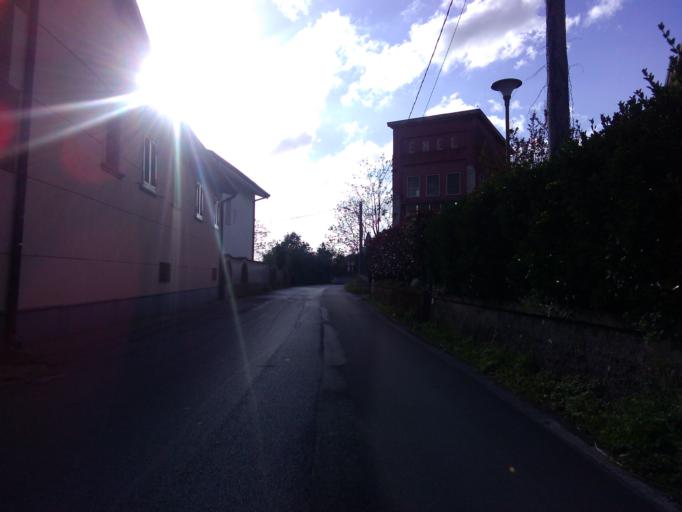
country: IT
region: Tuscany
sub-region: Provincia di Lucca
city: Strettoia
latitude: 43.9882
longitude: 10.1949
